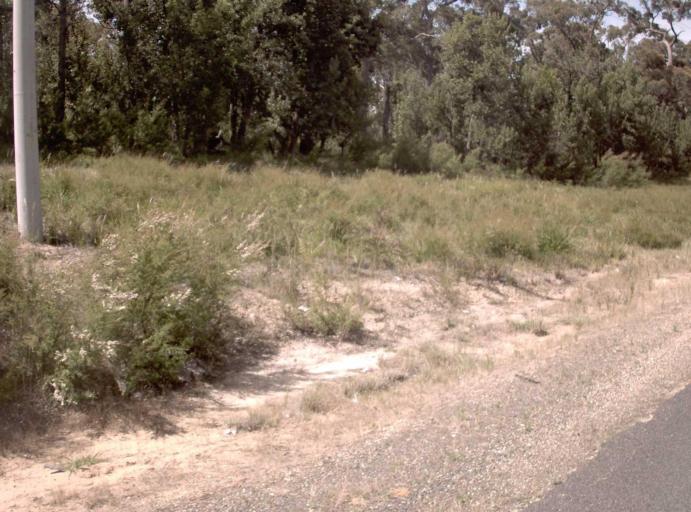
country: AU
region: Victoria
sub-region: Wellington
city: Sale
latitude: -37.9166
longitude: 147.2925
